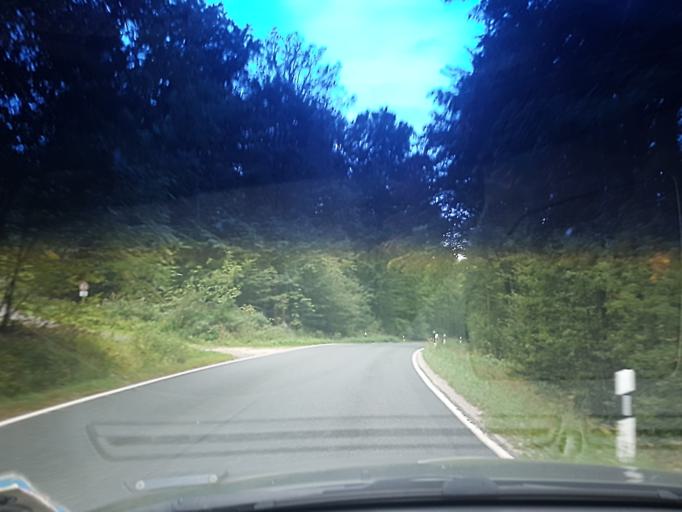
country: DE
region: Bavaria
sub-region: Regierungsbezirk Unterfranken
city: Michelau
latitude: 49.8591
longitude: 10.5057
